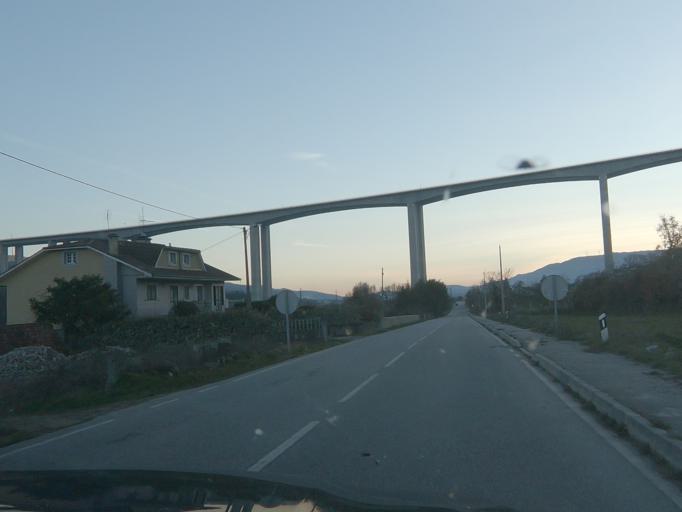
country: PT
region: Vila Real
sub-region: Vila Pouca de Aguiar
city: Vila Pouca de Aguiar
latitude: 41.4861
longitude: -7.6515
